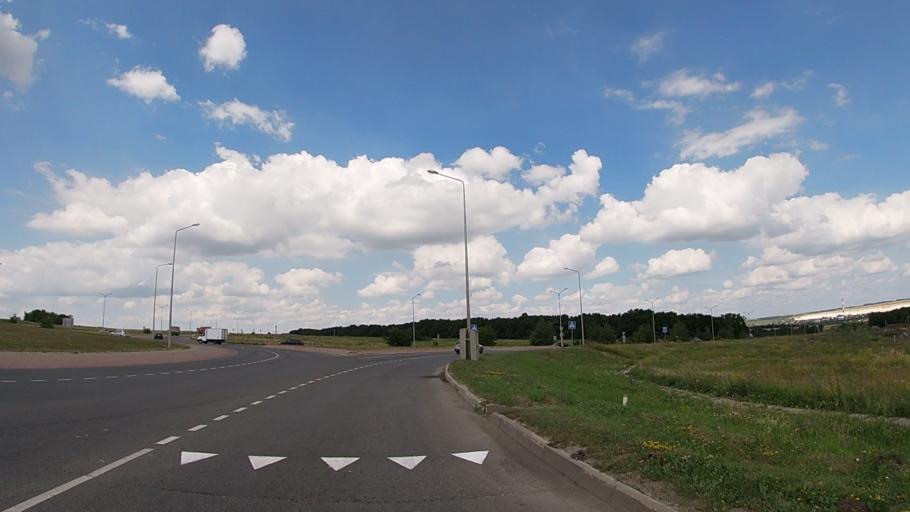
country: RU
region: Belgorod
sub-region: Belgorodskiy Rayon
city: Belgorod
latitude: 50.5937
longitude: 36.5316
